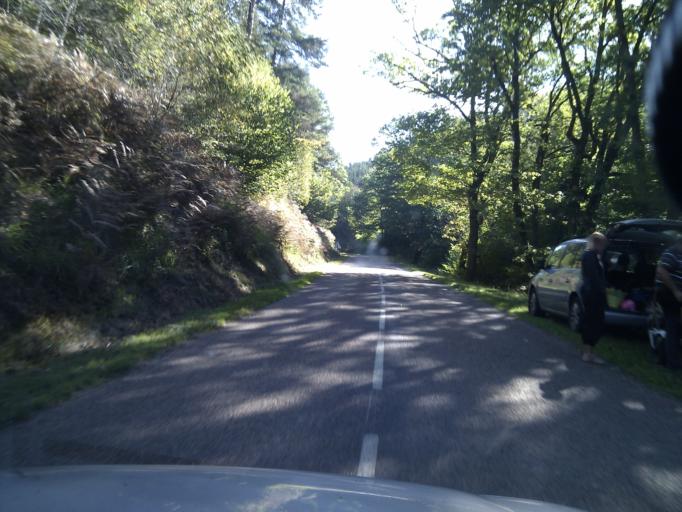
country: FR
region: Bourgogne
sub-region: Departement de la Cote-d'Or
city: Saulieu
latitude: 47.2845
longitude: 4.0410
